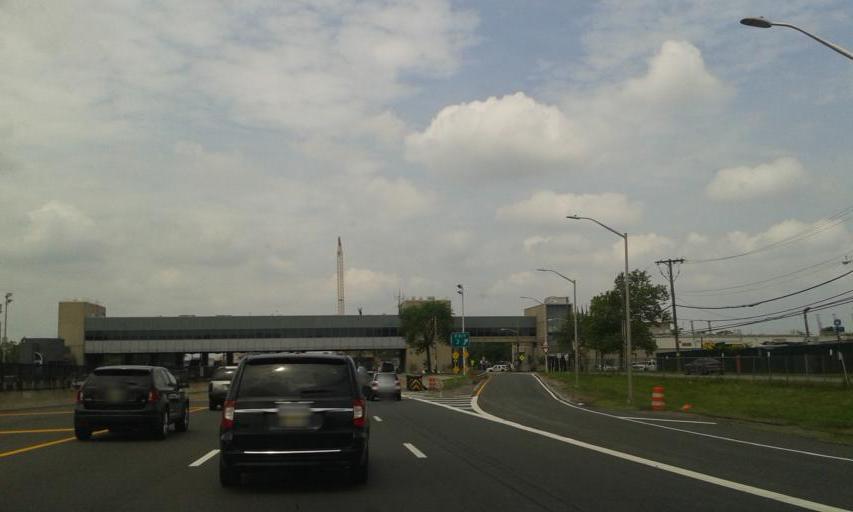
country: US
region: New York
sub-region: Richmond County
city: Bloomfield
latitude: 40.6270
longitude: -74.1803
